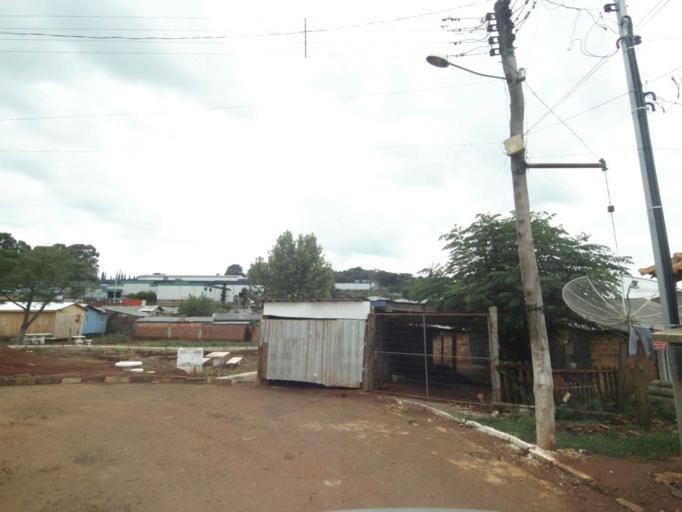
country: BR
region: Rio Grande do Sul
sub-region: Lagoa Vermelha
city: Lagoa Vermelha
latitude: -28.2268
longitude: -51.5144
